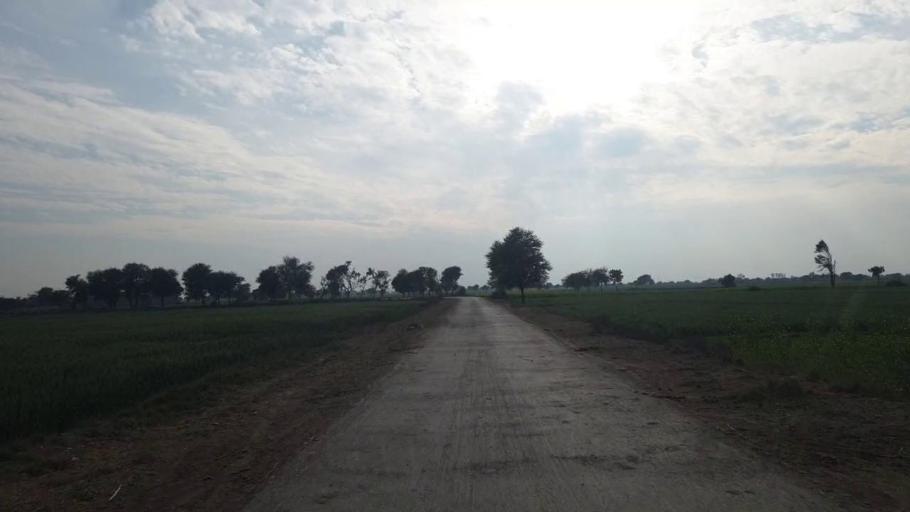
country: PK
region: Sindh
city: Shahpur Chakar
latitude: 26.0495
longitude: 68.5767
